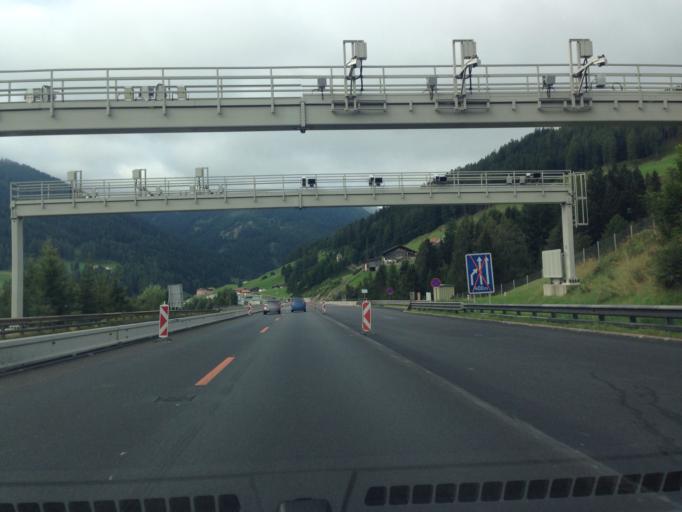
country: AT
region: Tyrol
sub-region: Politischer Bezirk Innsbruck Land
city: Gries am Brenner
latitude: 47.0439
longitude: 11.4789
